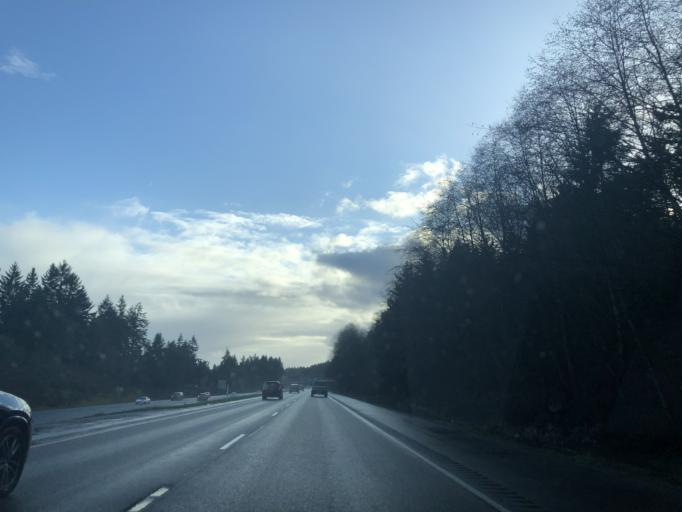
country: US
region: Washington
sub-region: Kitsap County
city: Chico
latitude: 47.6207
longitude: -122.7117
